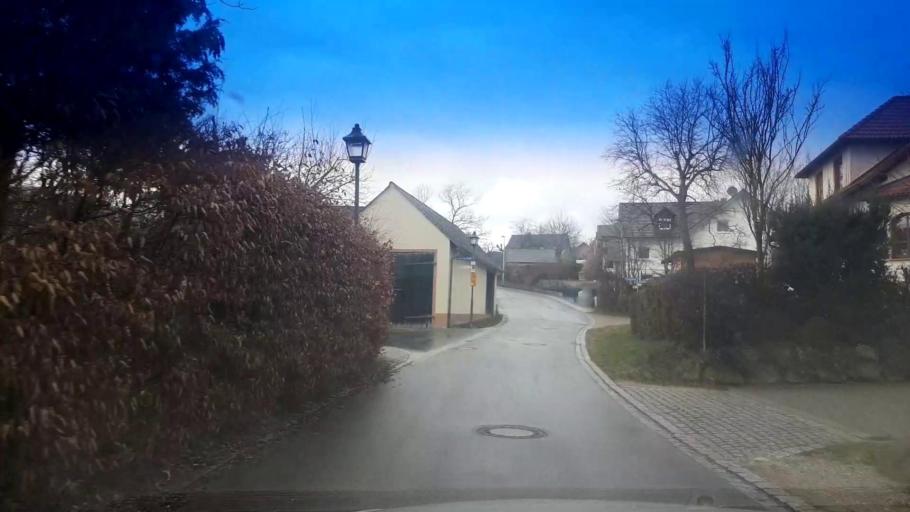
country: DE
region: Bavaria
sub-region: Upper Franconia
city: Litzendorf
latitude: 49.8689
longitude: 11.0241
